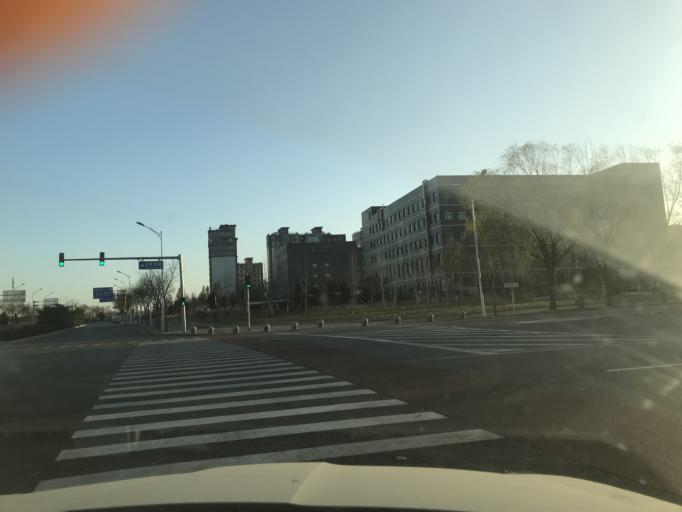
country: CN
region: Beijing
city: Xibeiwang
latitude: 40.0689
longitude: 116.2511
